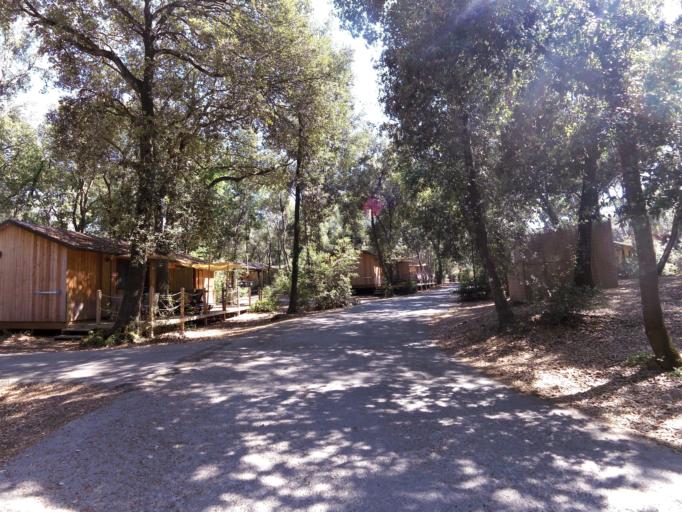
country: IT
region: Tuscany
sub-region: Provincia di Livorno
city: Donoratico
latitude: 43.1543
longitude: 10.5446
